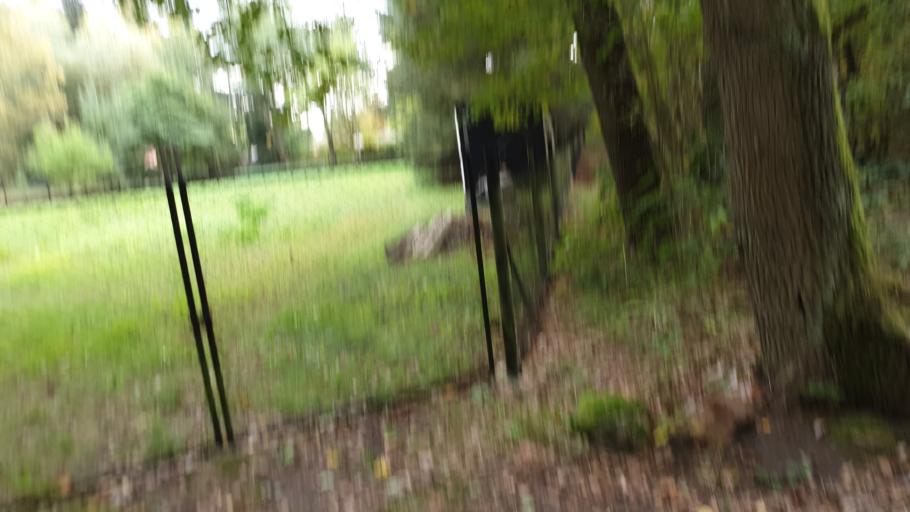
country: DE
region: Brandenburg
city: Liepe
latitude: 52.8634
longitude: 13.9473
